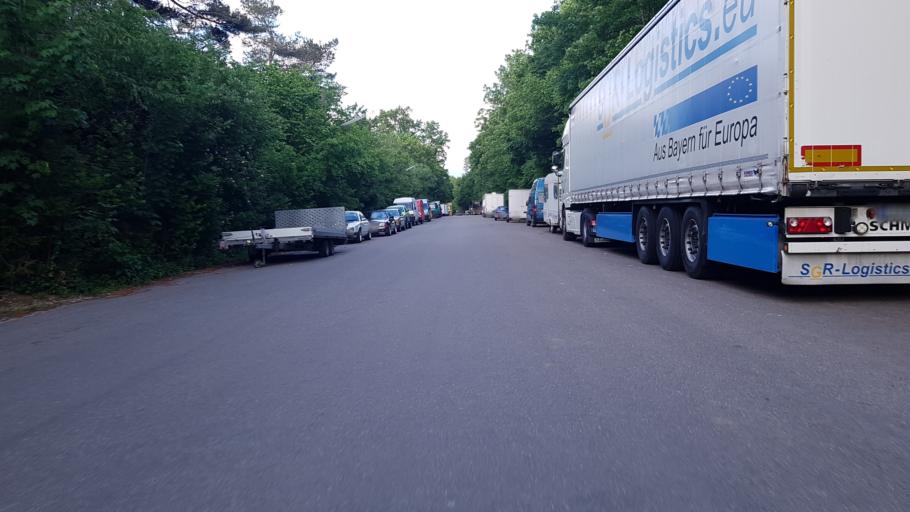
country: DE
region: Bavaria
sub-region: Upper Bavaria
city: Neuried
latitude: 48.1029
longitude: 11.4838
